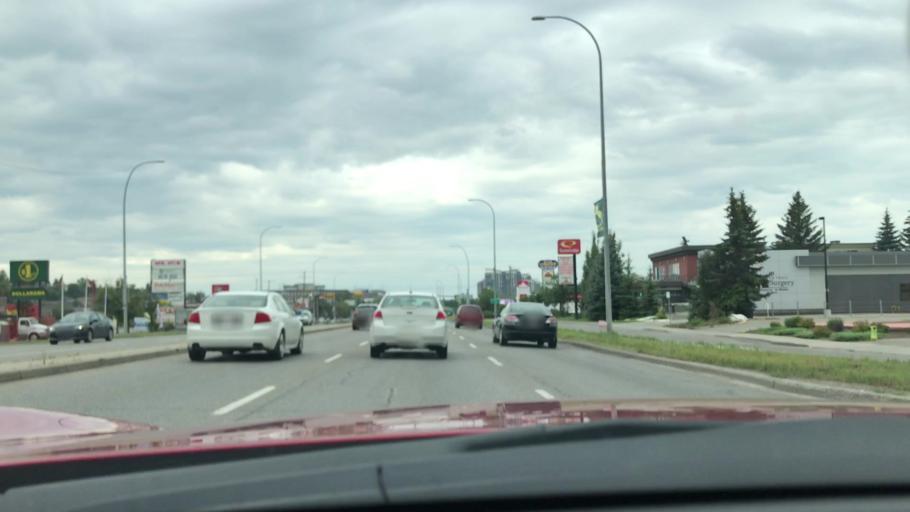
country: CA
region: Alberta
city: Calgary
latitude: 50.9878
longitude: -114.0717
